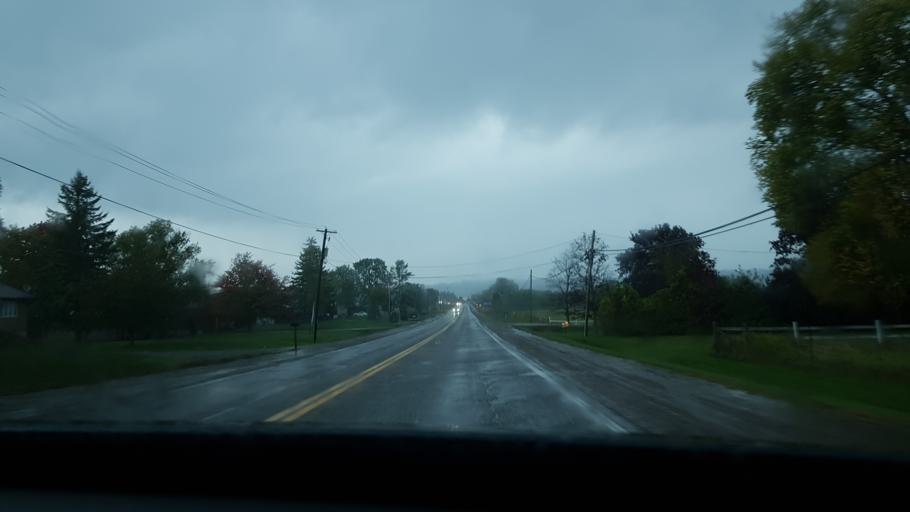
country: CA
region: Ontario
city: Peterborough
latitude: 44.3855
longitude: -78.4080
